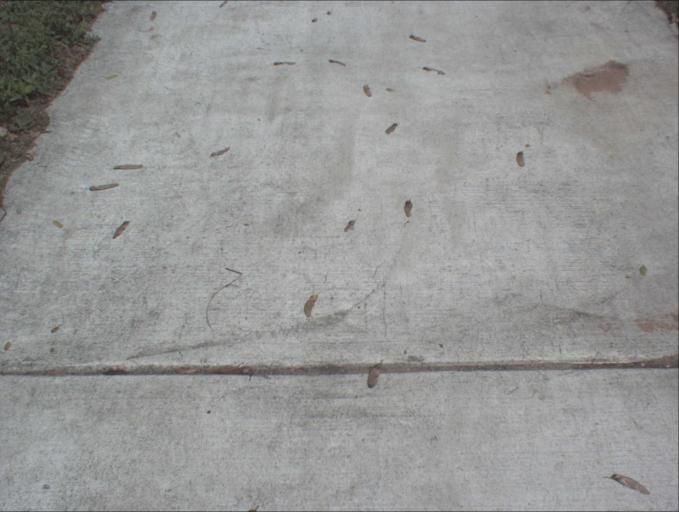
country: AU
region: Queensland
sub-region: Logan
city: Park Ridge South
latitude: -27.7402
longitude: 153.0266
